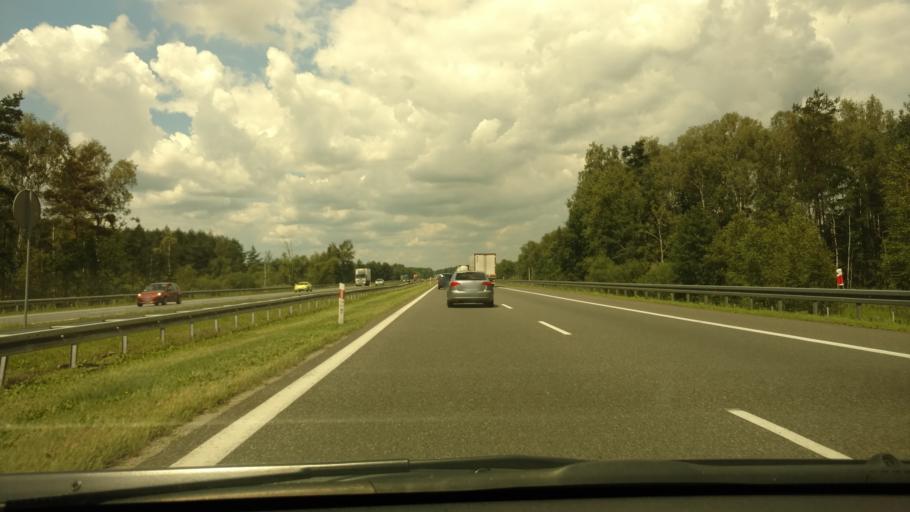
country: PL
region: Lesser Poland Voivodeship
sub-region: Powiat chrzanowski
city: Bolecin
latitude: 50.1183
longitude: 19.4984
